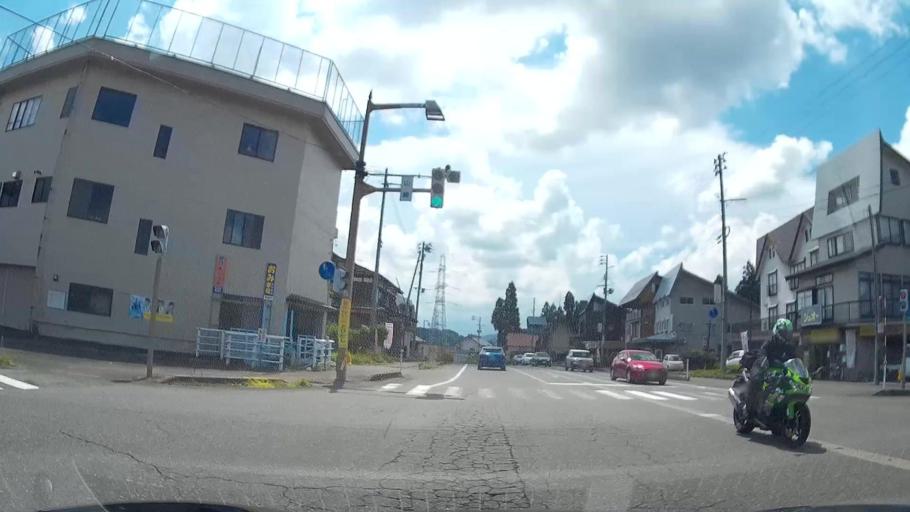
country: JP
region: Niigata
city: Tokamachi
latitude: 37.0511
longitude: 138.6950
